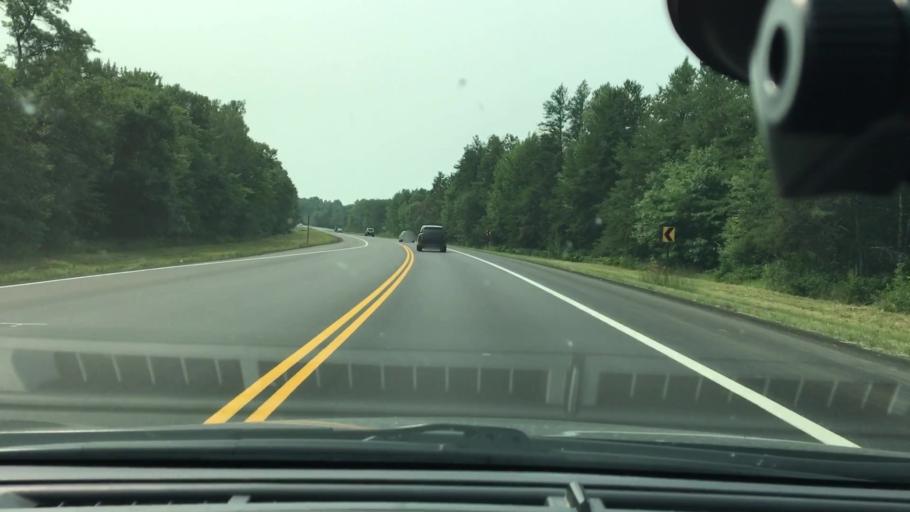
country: US
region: Minnesota
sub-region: Crow Wing County
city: Brainerd
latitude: 46.4238
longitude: -94.1784
